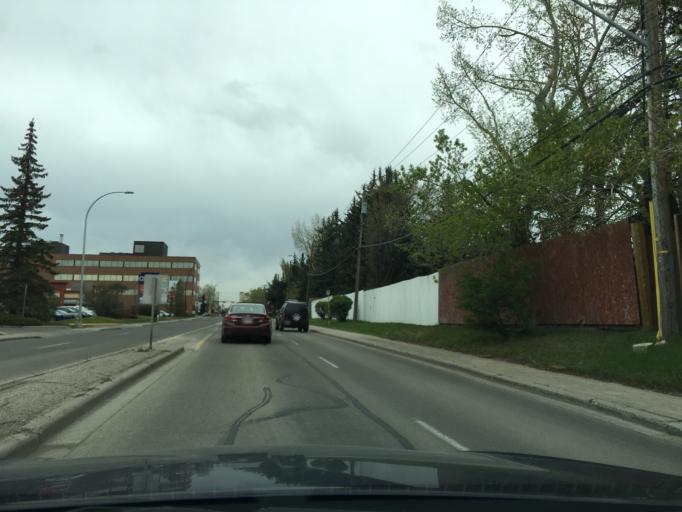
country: CA
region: Alberta
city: Calgary
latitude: 50.9587
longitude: -114.0688
